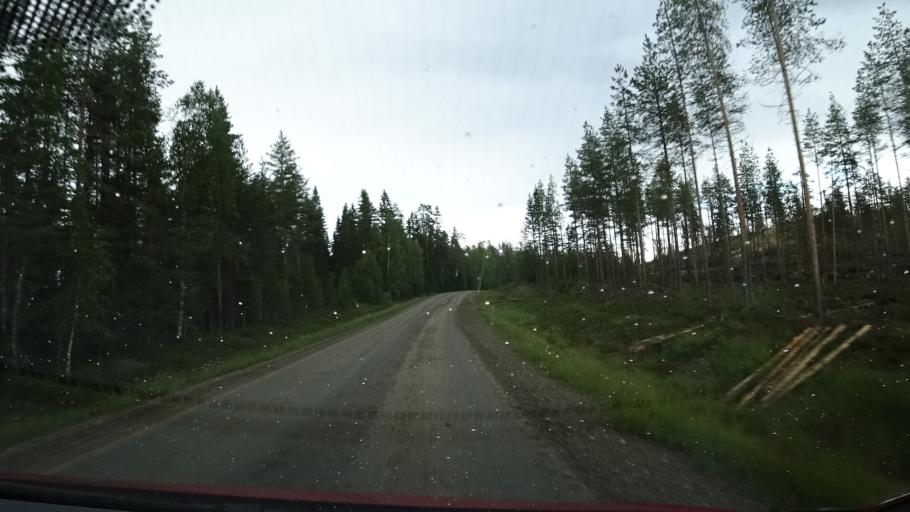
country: FI
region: Kainuu
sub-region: Kehys-Kainuu
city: Kuhmo
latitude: 63.9504
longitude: 29.2171
